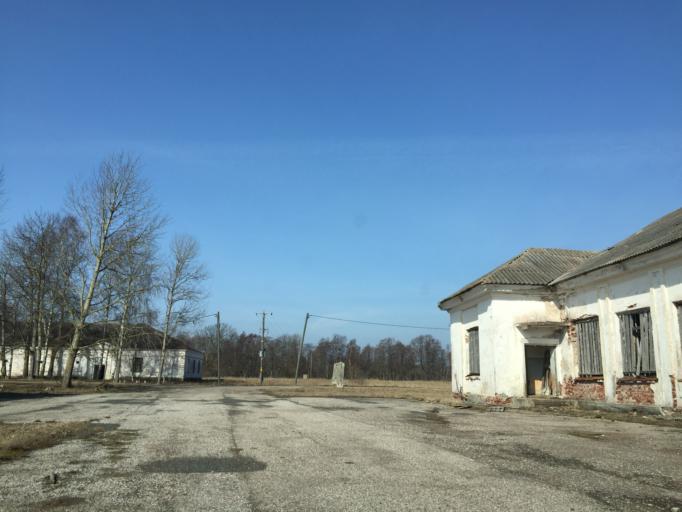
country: LV
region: Dundaga
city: Dundaga
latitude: 57.9349
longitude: 22.0699
